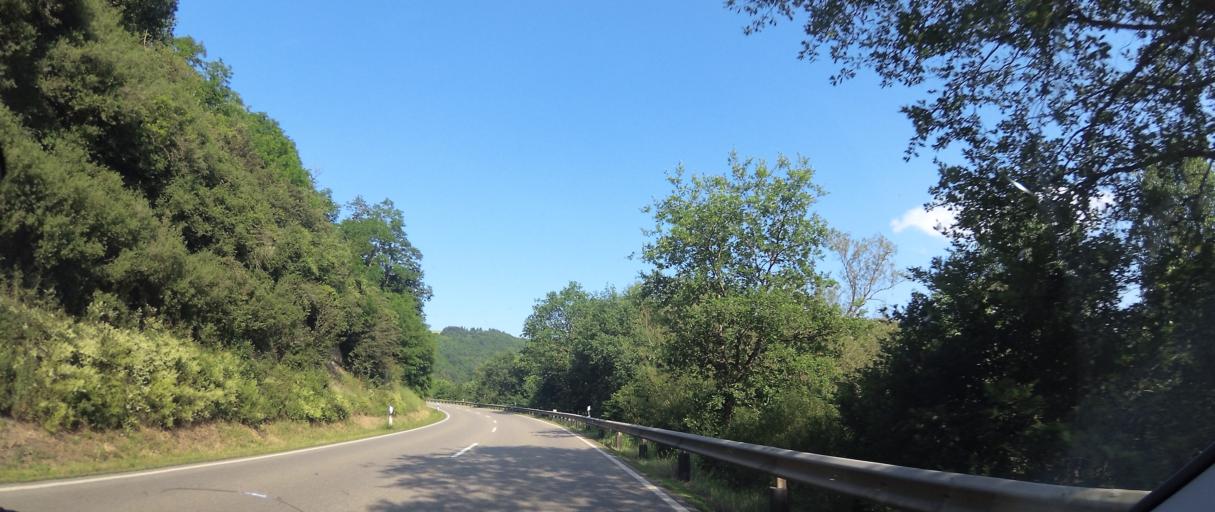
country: DE
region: Rheinland-Pfalz
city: Wiesweiler
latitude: 49.6288
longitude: 7.5621
